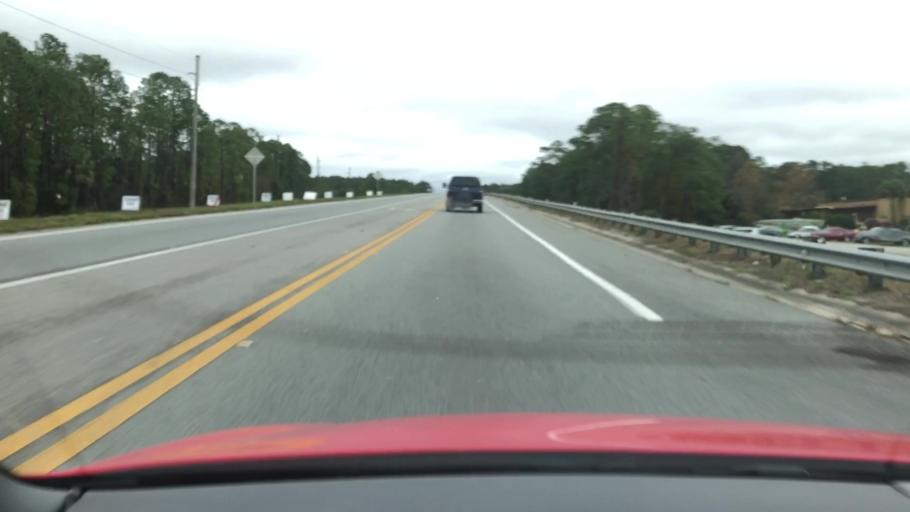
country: US
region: Florida
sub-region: Volusia County
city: West DeLand
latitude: 29.0234
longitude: -81.3584
